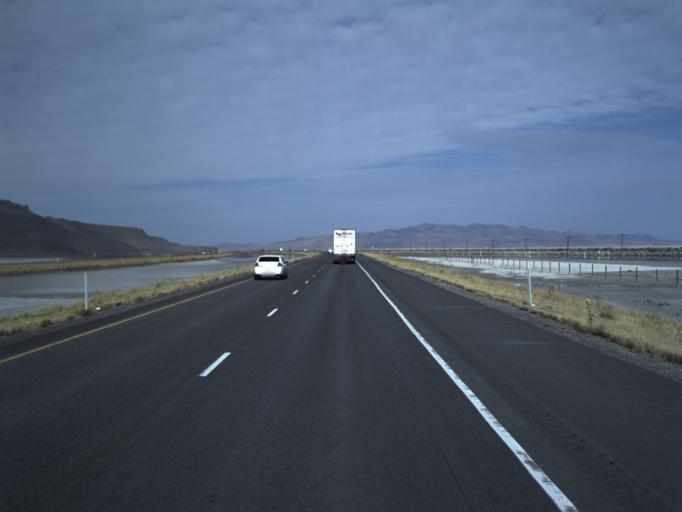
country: US
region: Utah
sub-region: Tooele County
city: Grantsville
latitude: 40.7183
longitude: -112.5492
